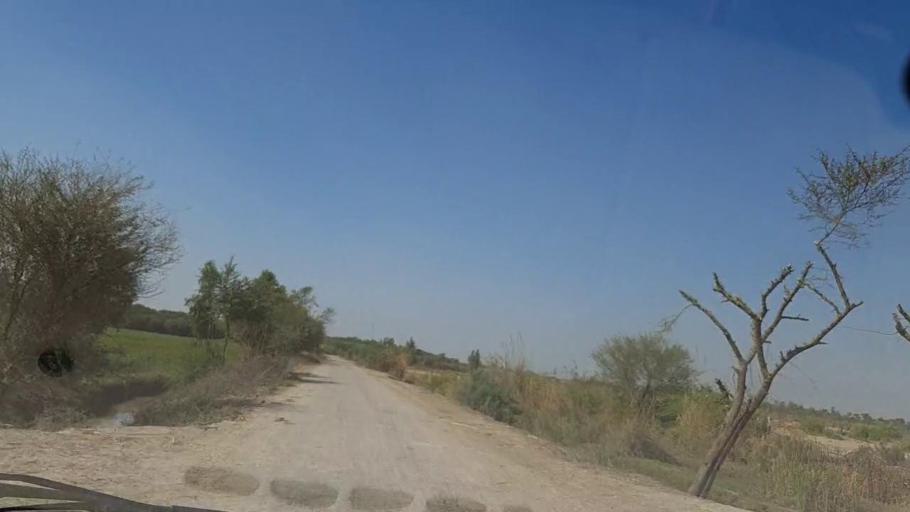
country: PK
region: Sindh
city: Mirwah Gorchani
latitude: 25.3814
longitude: 68.9743
